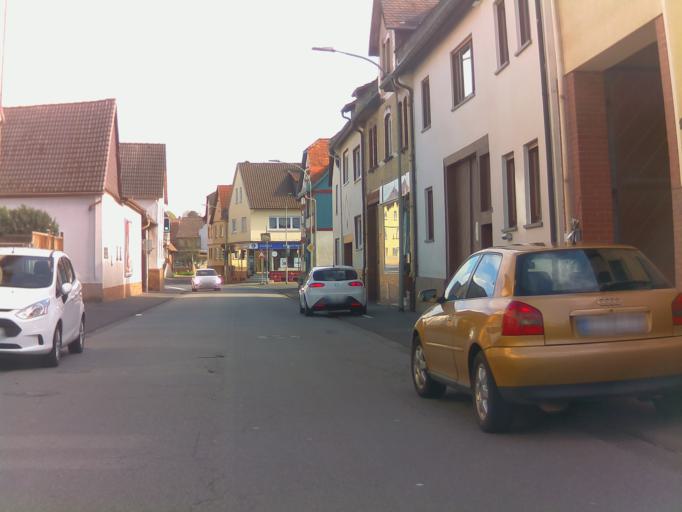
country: DE
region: Hesse
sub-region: Regierungsbezirk Giessen
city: Langgons
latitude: 50.4996
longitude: 8.6588
